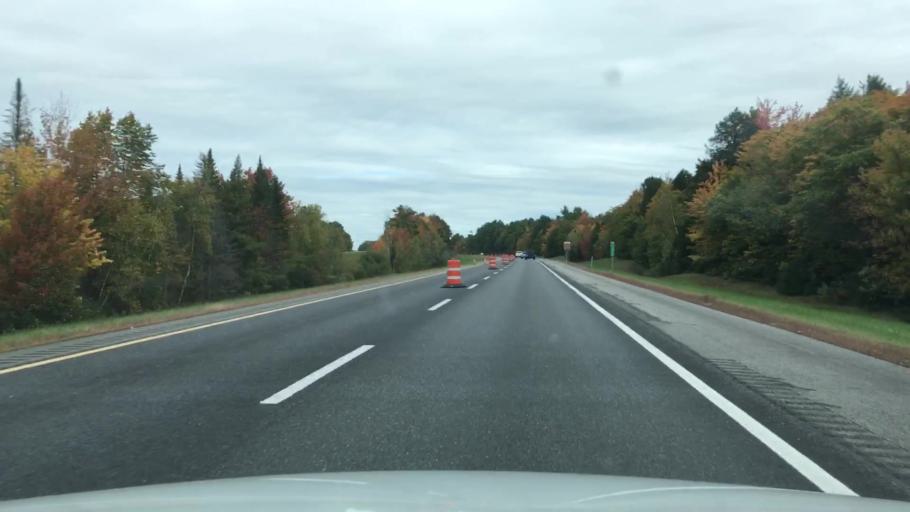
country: US
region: Maine
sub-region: Sagadahoc County
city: Richmond
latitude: 44.1181
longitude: -69.8534
